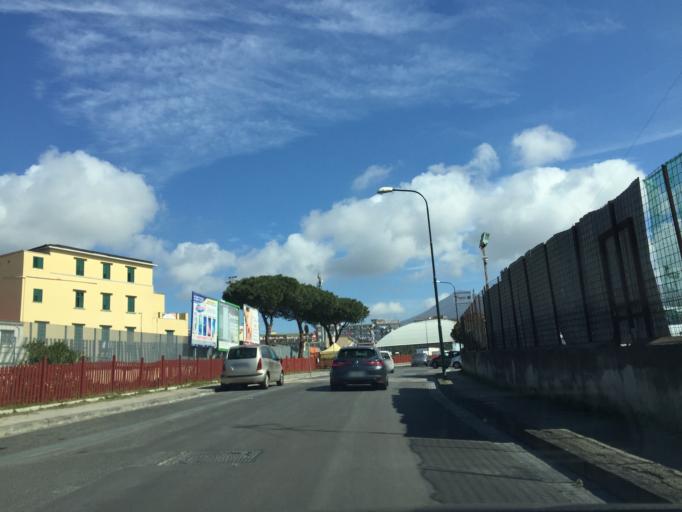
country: IT
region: Campania
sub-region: Provincia di Napoli
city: Portici
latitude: 40.8248
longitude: 14.3311
